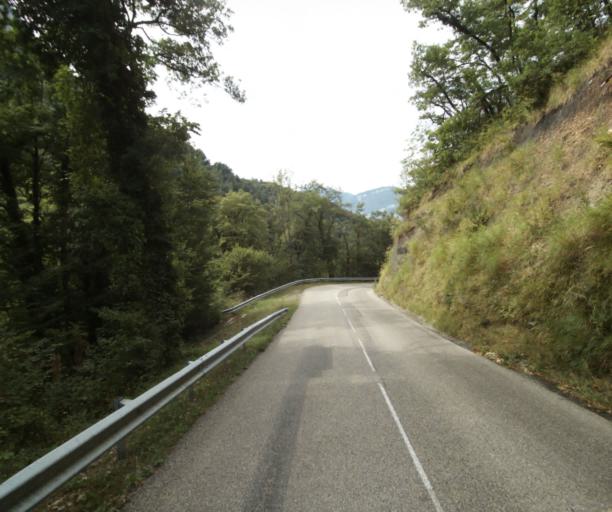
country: FR
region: Rhone-Alpes
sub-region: Departement de l'Isere
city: Saint-Egreve
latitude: 45.2493
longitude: 5.7008
